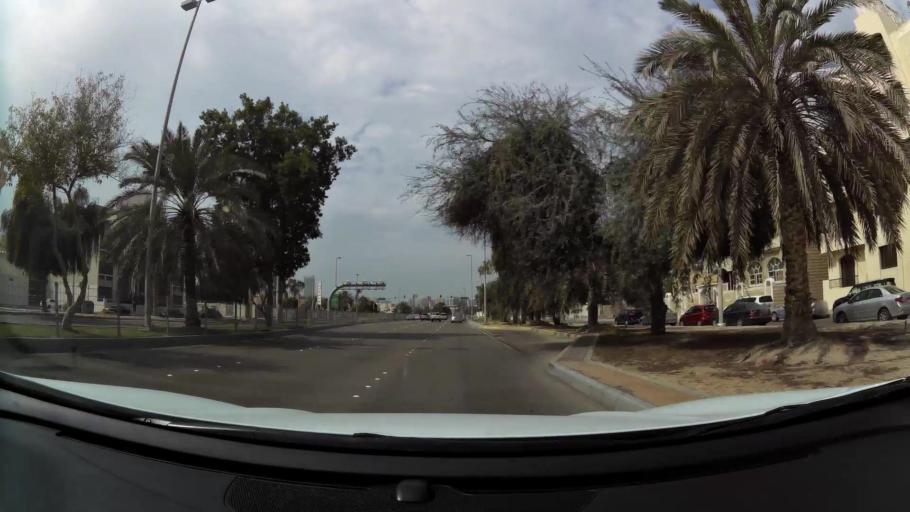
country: AE
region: Abu Dhabi
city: Abu Dhabi
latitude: 24.4582
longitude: 54.3593
